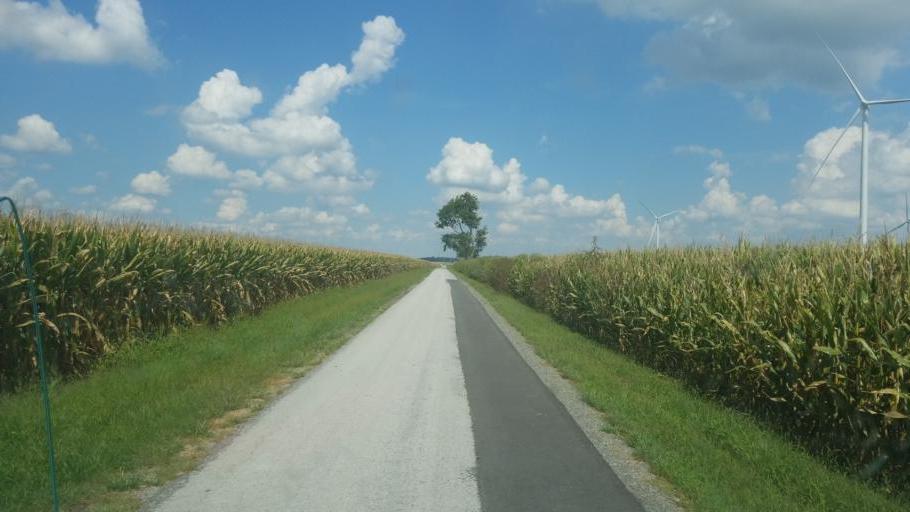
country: US
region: Ohio
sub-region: Hardin County
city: Ada
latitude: 40.7843
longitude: -83.7478
